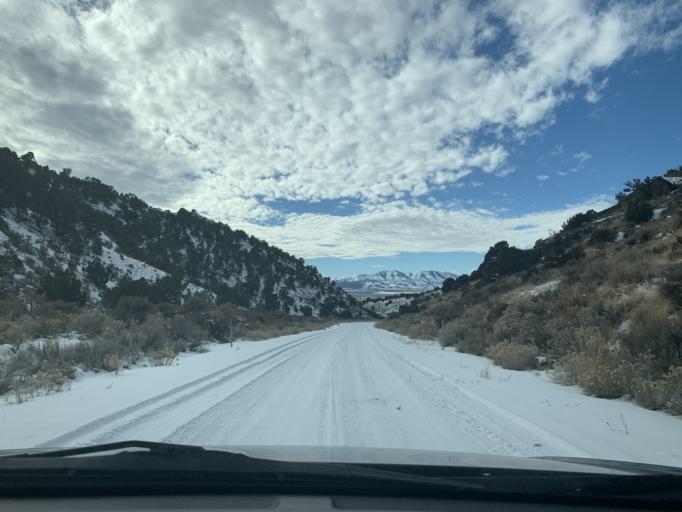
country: US
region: Utah
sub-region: Tooele County
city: Tooele
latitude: 40.3104
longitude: -112.2480
